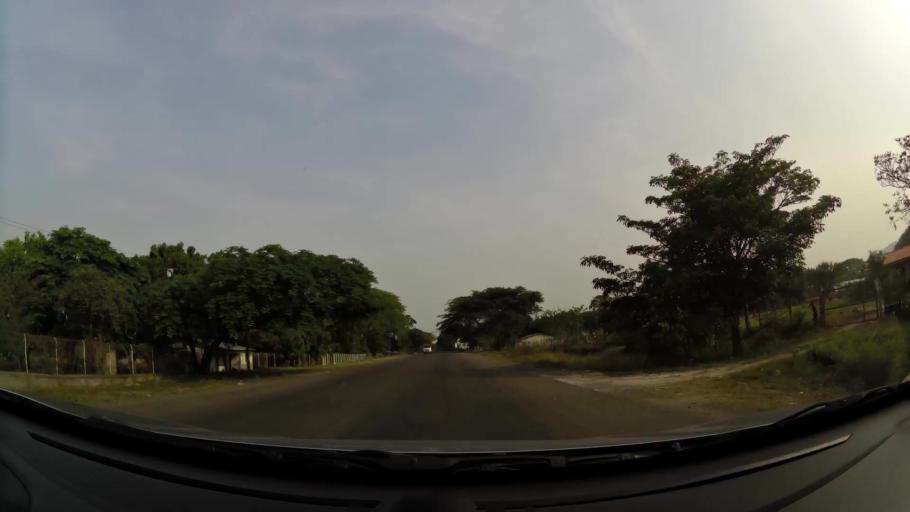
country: HN
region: Comayagua
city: Flores
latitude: 14.2788
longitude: -87.5629
